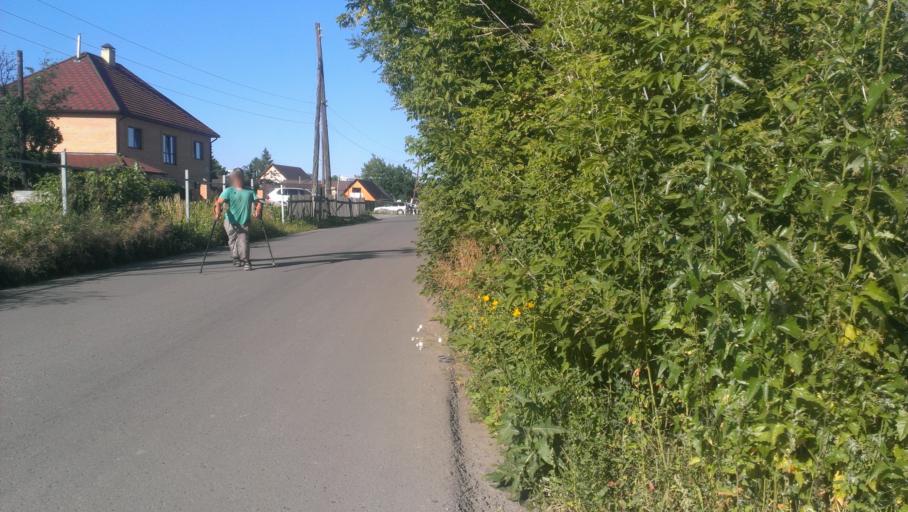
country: RU
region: Altai Krai
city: Novosilikatnyy
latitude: 53.3202
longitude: 83.6781
